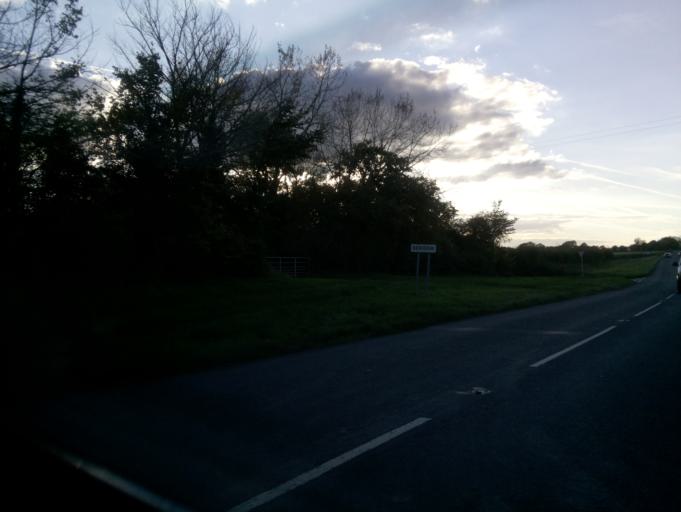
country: GB
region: England
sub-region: Worcestershire
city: Upton upon Severn
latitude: 52.0117
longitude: -2.2861
